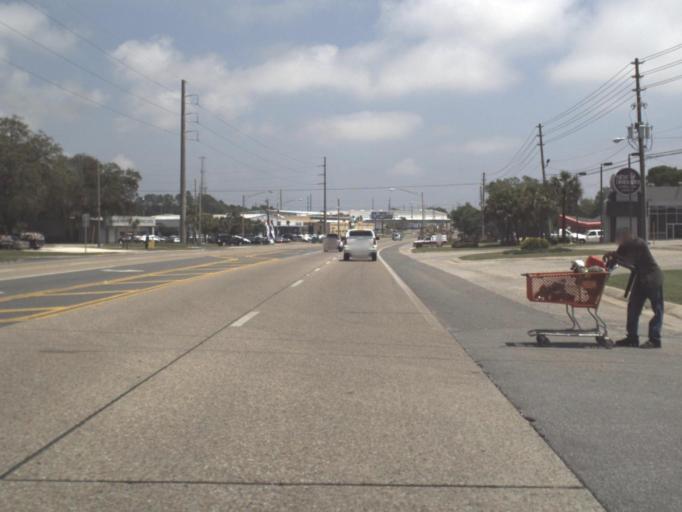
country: US
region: Florida
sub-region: Escambia County
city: West Pensacola
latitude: 30.4118
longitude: -87.2544
